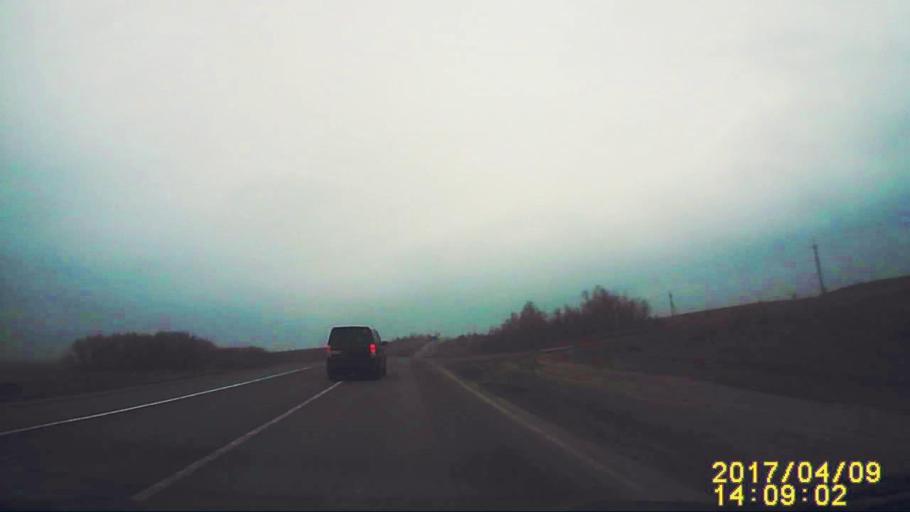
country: RU
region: Ulyanovsk
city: Silikatnyy
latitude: 54.0248
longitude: 48.2142
